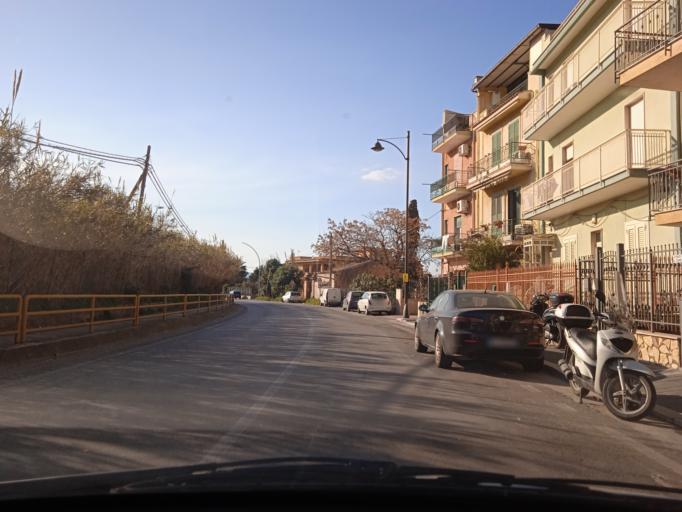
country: IT
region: Sicily
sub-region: Palermo
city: Ficarazzi
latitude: 38.0886
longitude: 13.4521
